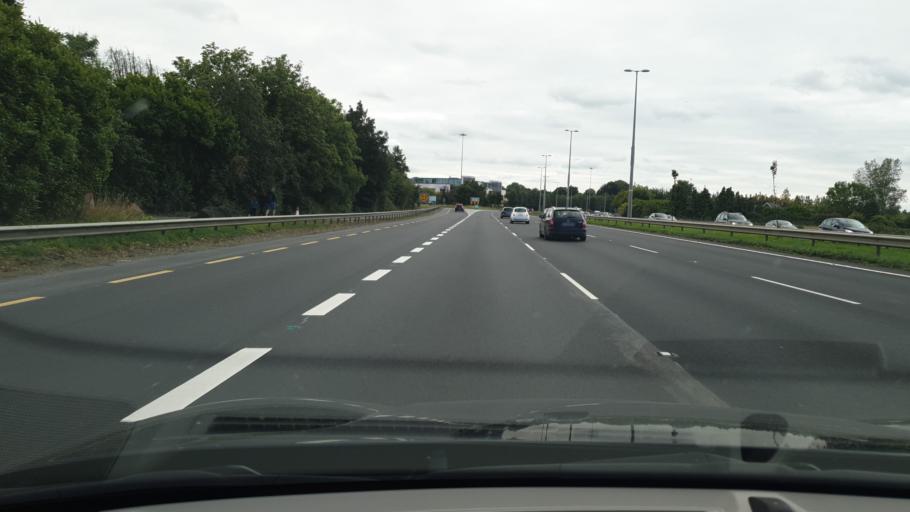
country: IE
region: Leinster
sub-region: South Dublin
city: Saggart
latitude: 53.2864
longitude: -6.4524
